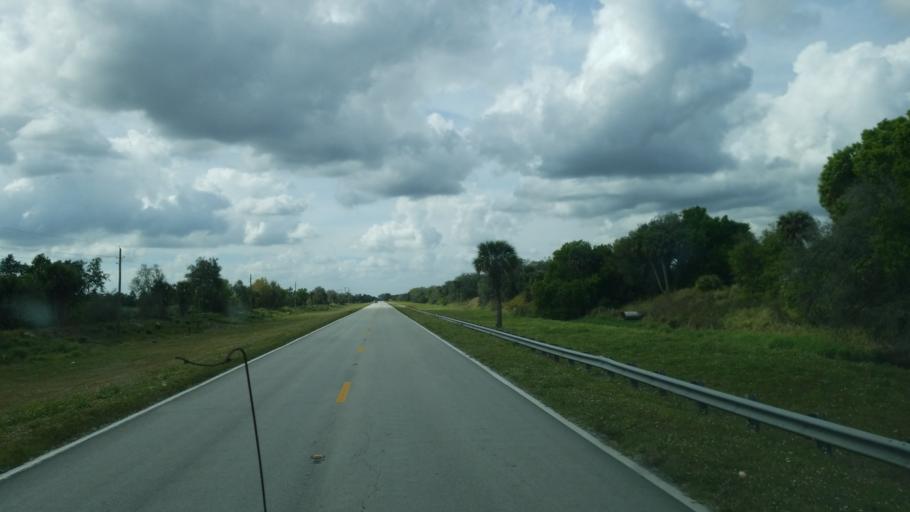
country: US
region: Florida
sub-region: Indian River County
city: West Vero Corridor
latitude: 27.4486
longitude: -80.6478
